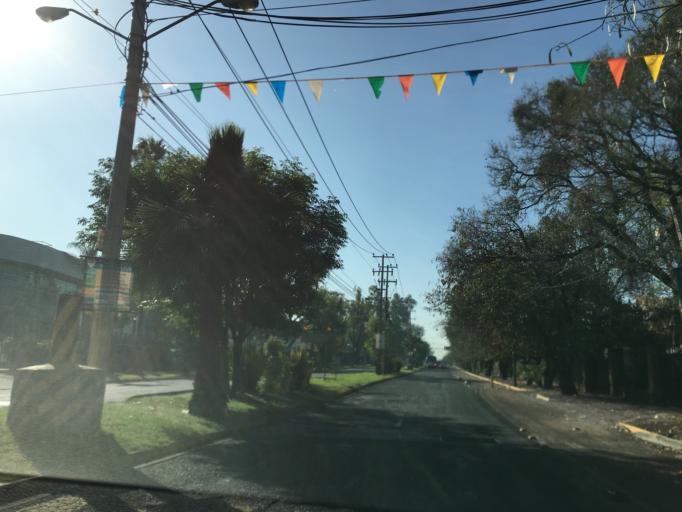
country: MX
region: Jalisco
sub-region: Tlajomulco de Zuniga
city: La Tijera
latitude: 20.6171
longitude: -103.4220
